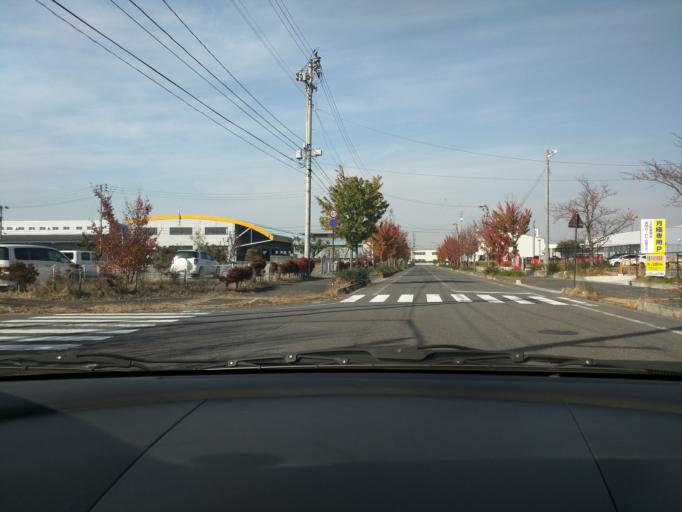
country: JP
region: Fukushima
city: Kitakata
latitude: 37.5242
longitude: 139.9155
